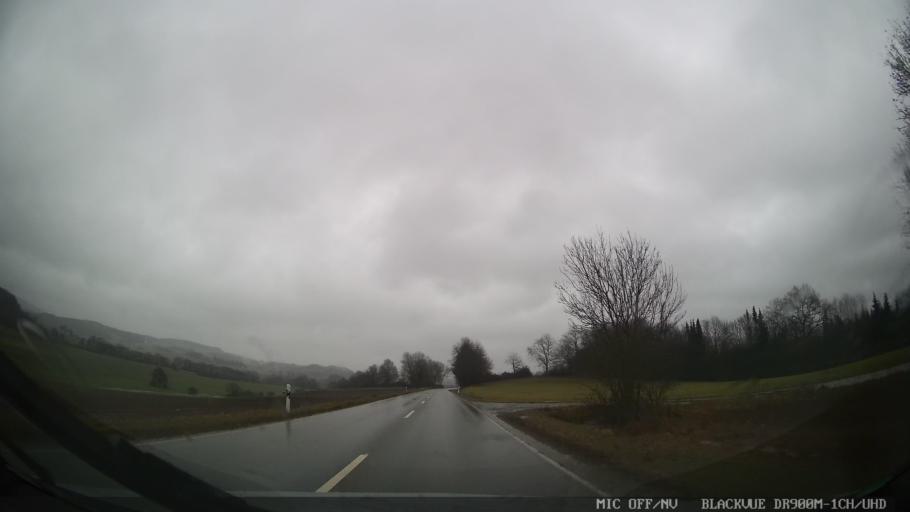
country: DE
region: Rheinland-Pfalz
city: Dambach
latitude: 49.6451
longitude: 7.1373
